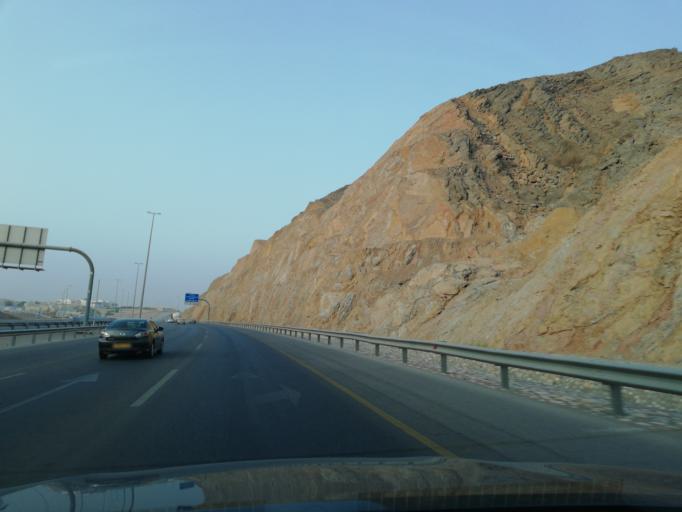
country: OM
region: Muhafazat Masqat
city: Bawshar
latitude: 23.5853
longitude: 58.4556
